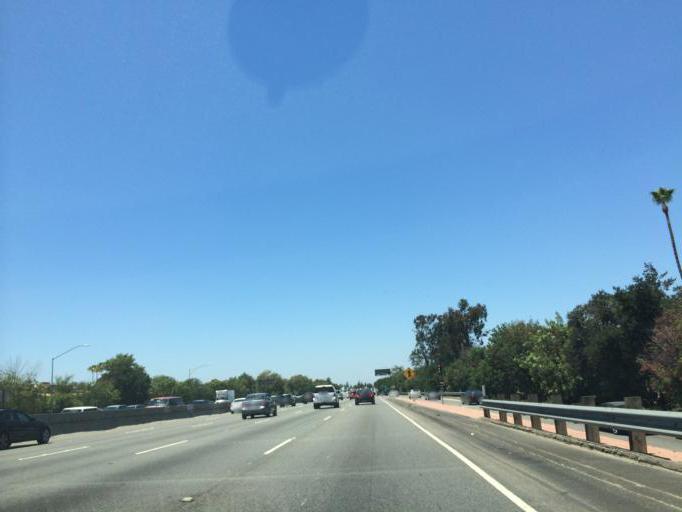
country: US
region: California
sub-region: Los Angeles County
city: Northridge
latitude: 34.1713
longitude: -118.5197
